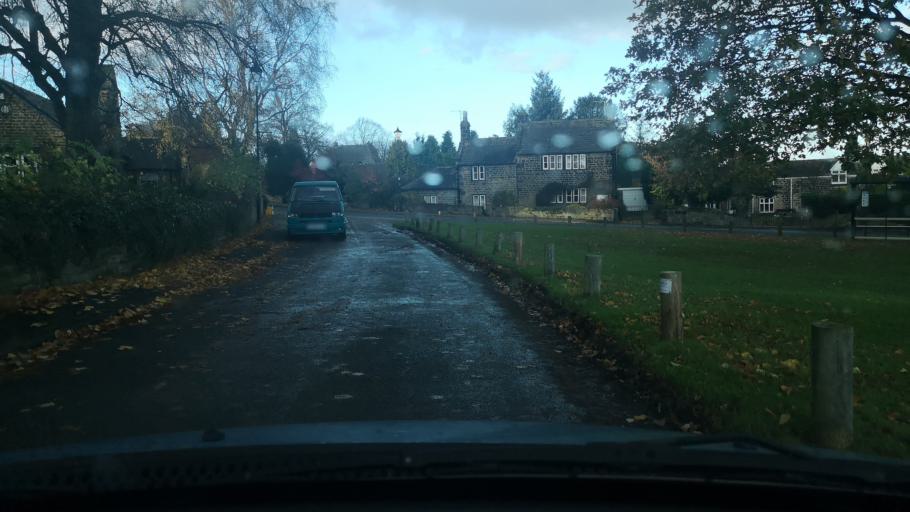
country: GB
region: England
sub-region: City and Borough of Wakefield
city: Woolley
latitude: 53.6142
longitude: -1.5164
